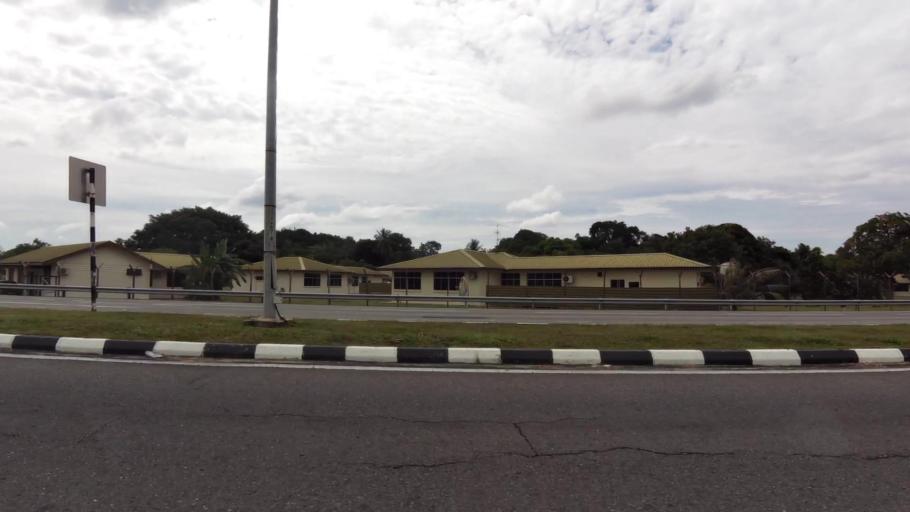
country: BN
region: Brunei and Muara
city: Bandar Seri Begawan
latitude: 4.9080
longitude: 114.9078
